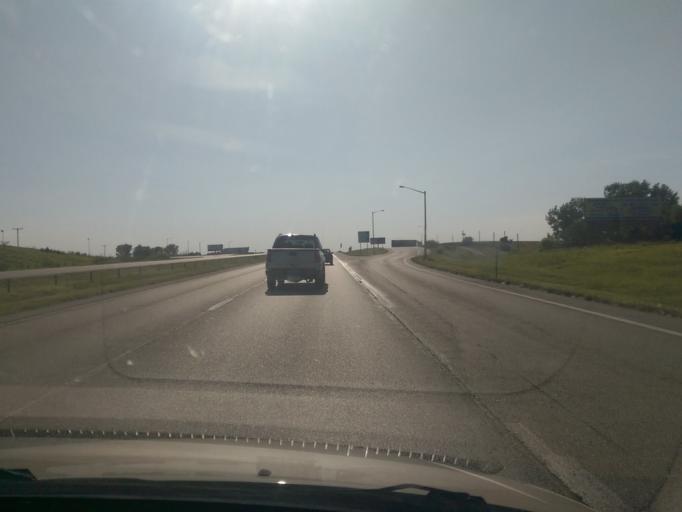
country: US
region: Missouri
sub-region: Lafayette County
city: Odessa
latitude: 39.0093
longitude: -93.9922
